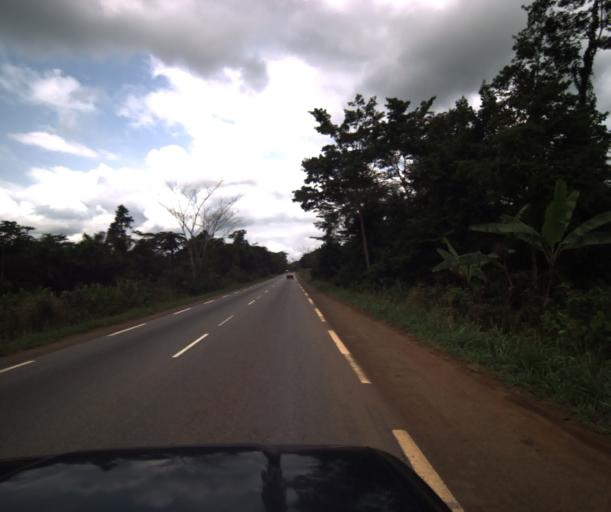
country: CM
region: Centre
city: Eseka
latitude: 3.8431
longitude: 10.9775
